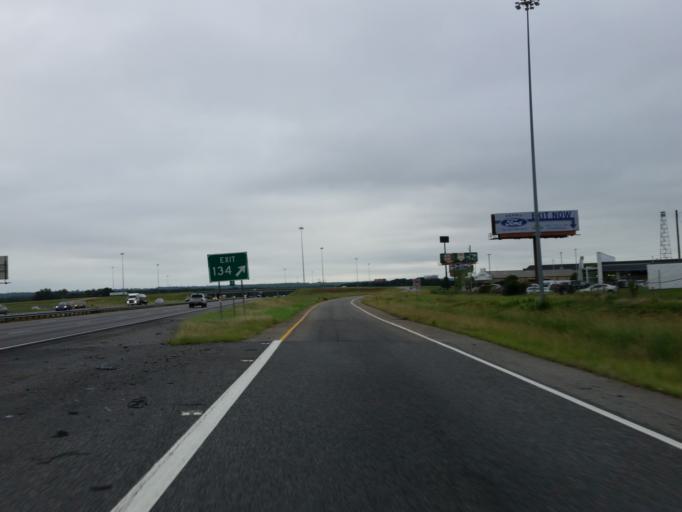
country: US
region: Georgia
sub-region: Houston County
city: Perry
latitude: 32.4384
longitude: -83.7562
